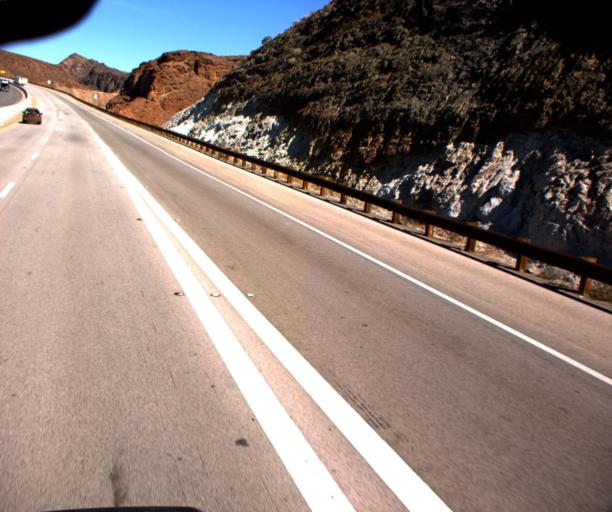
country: US
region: Nevada
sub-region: Clark County
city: Boulder City
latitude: 36.0056
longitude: -114.7249
